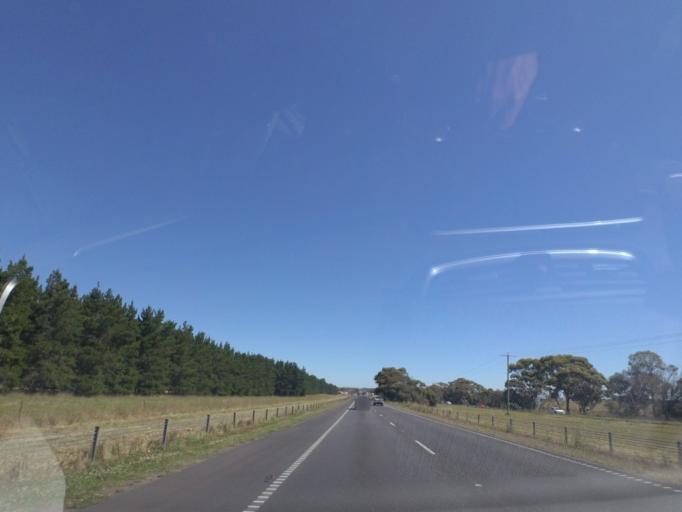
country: AU
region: Victoria
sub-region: Hume
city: Craigieburn
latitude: -37.5195
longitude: 144.9490
